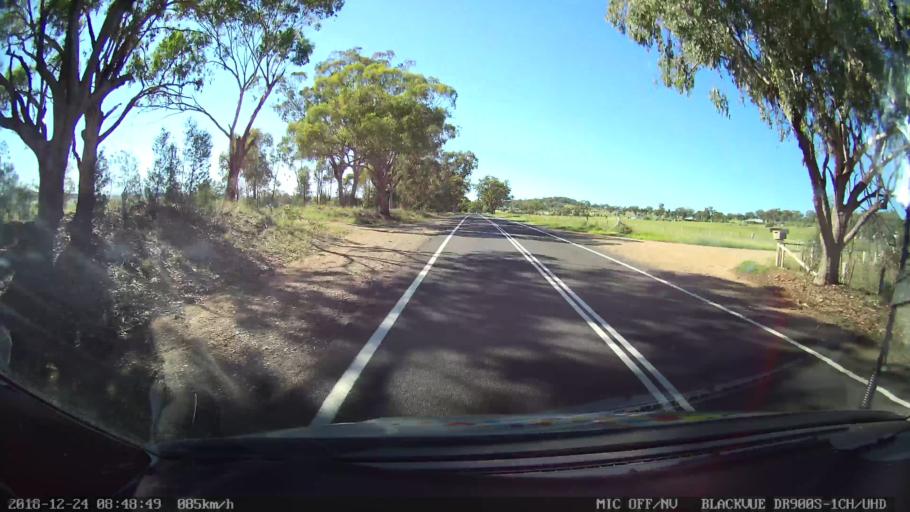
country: AU
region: New South Wales
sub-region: Liverpool Plains
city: Quirindi
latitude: -31.4603
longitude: 150.6486
